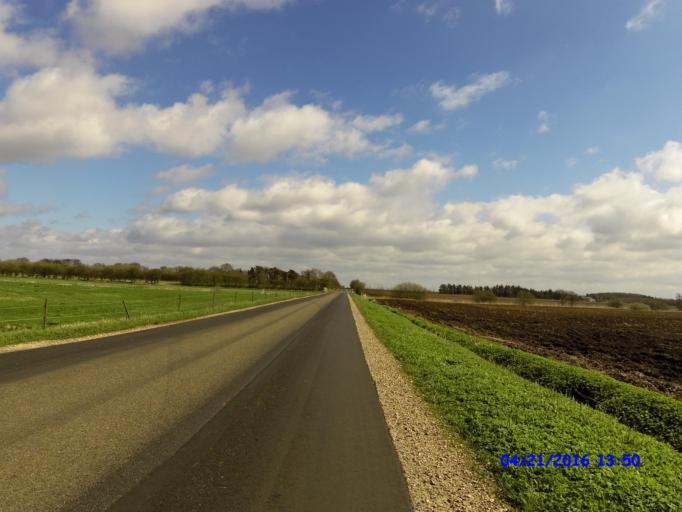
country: DK
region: South Denmark
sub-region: Haderslev Kommune
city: Gram
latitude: 55.2450
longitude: 8.9931
